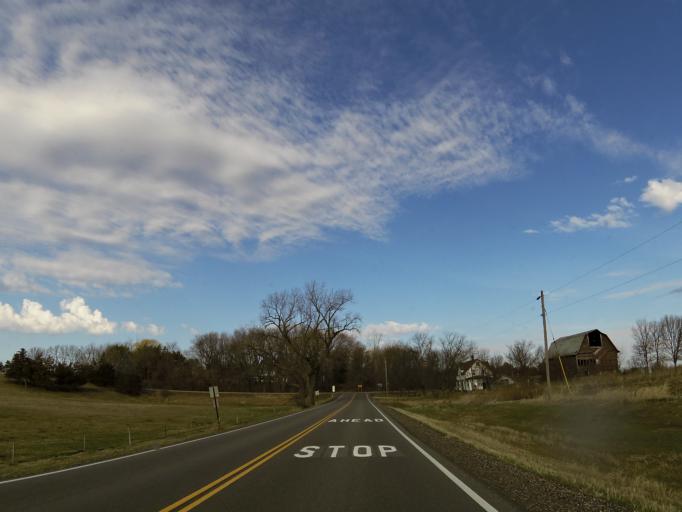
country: US
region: Minnesota
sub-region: Dakota County
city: Hastings
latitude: 44.8190
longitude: -92.8607
